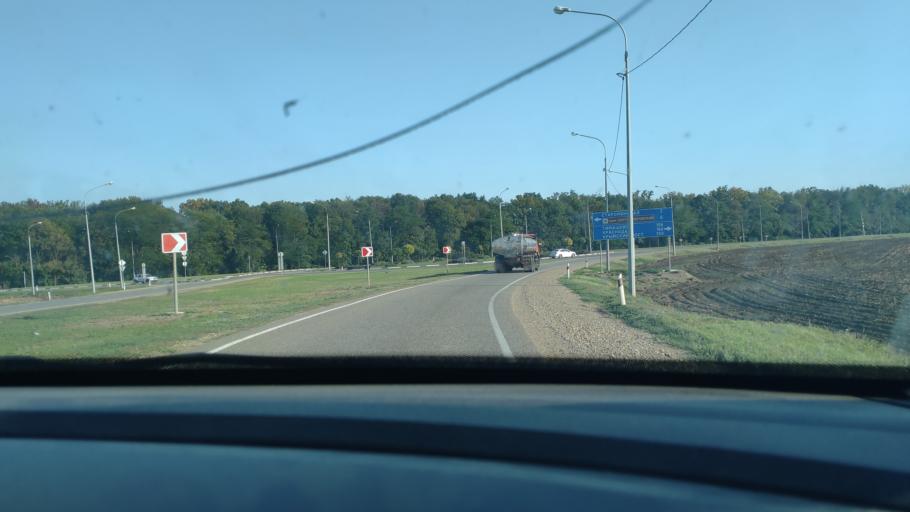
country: RU
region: Krasnodarskiy
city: Starominskaya
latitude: 46.4936
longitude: 39.0581
